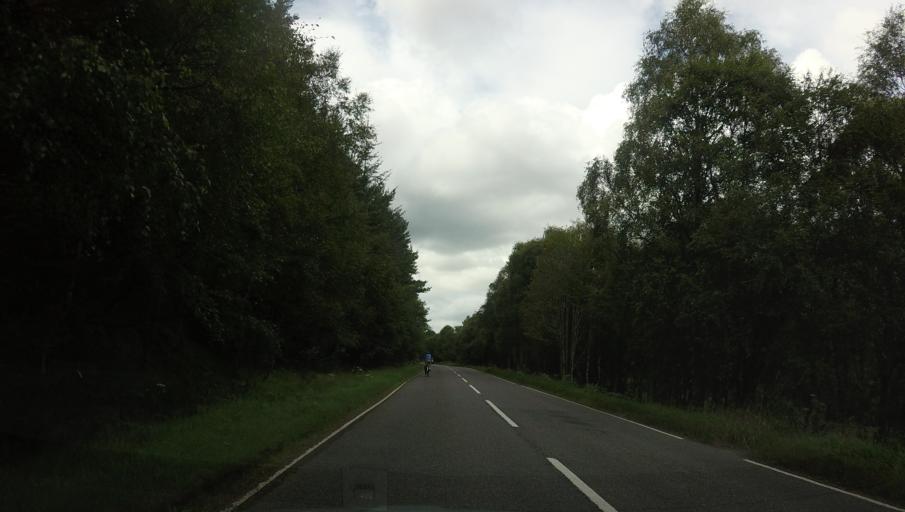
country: GB
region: Scotland
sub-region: Aberdeenshire
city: Torphins
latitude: 57.0642
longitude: -2.5913
